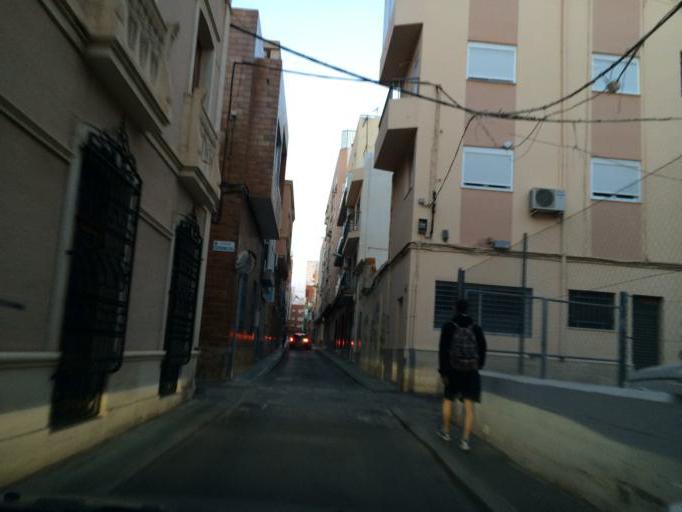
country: ES
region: Andalusia
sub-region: Provincia de Almeria
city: Almeria
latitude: 36.8435
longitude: -2.4632
